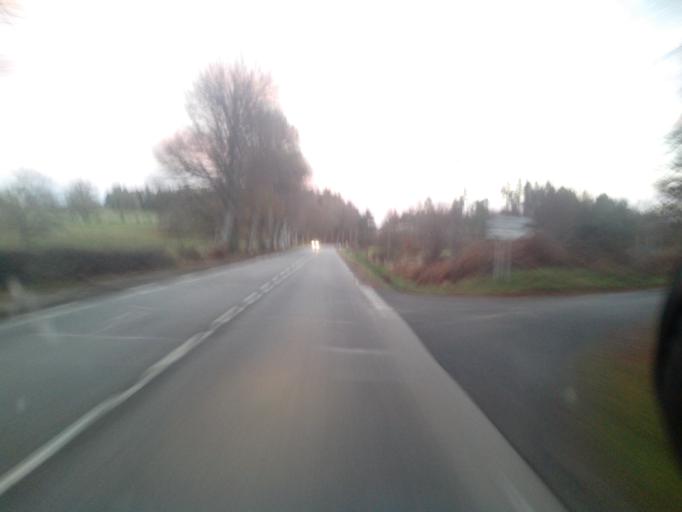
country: FR
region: Limousin
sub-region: Departement de la Correze
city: Meymac
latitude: 45.5139
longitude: 2.1827
